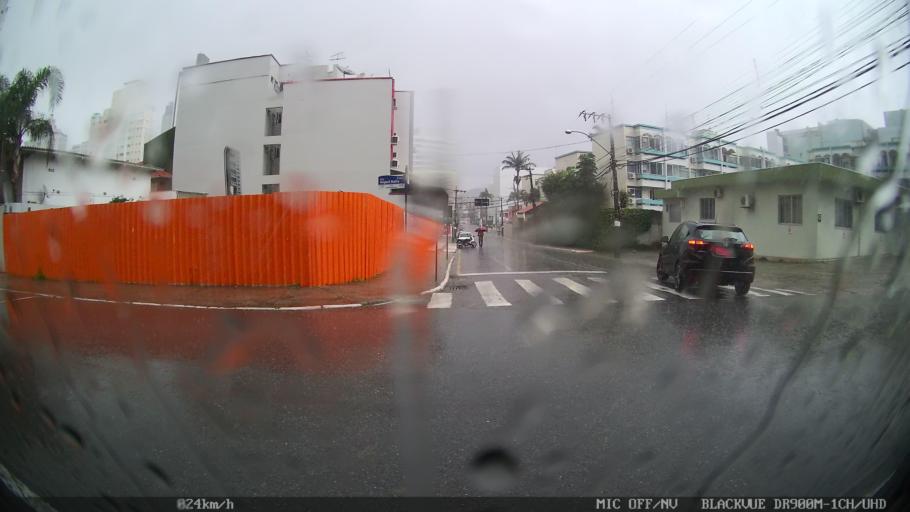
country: BR
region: Santa Catarina
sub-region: Balneario Camboriu
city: Balneario Camboriu
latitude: -26.9698
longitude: -48.6375
